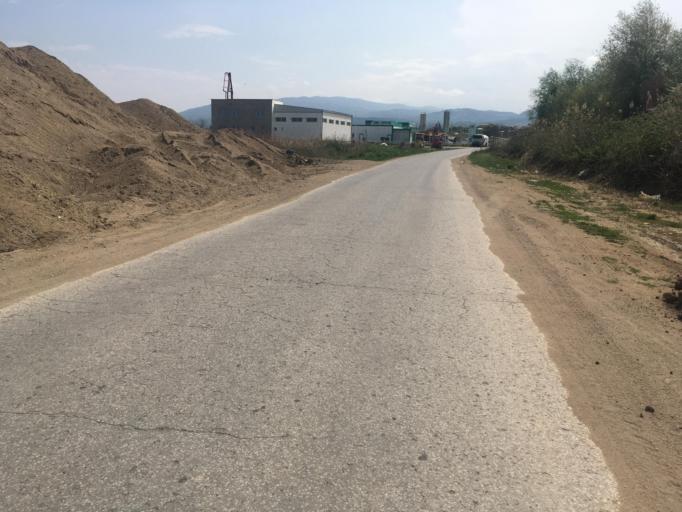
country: MK
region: Karbinci
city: Karbinci
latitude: 41.8004
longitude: 22.2172
